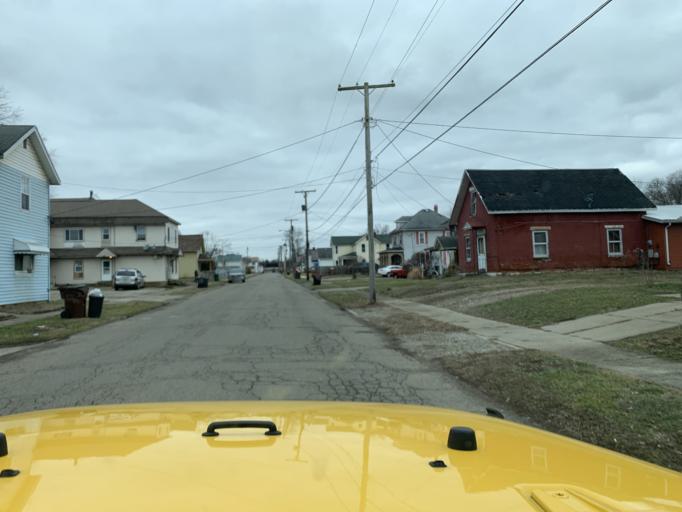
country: US
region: Ohio
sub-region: Licking County
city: Newark
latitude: 40.0495
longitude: -82.4059
